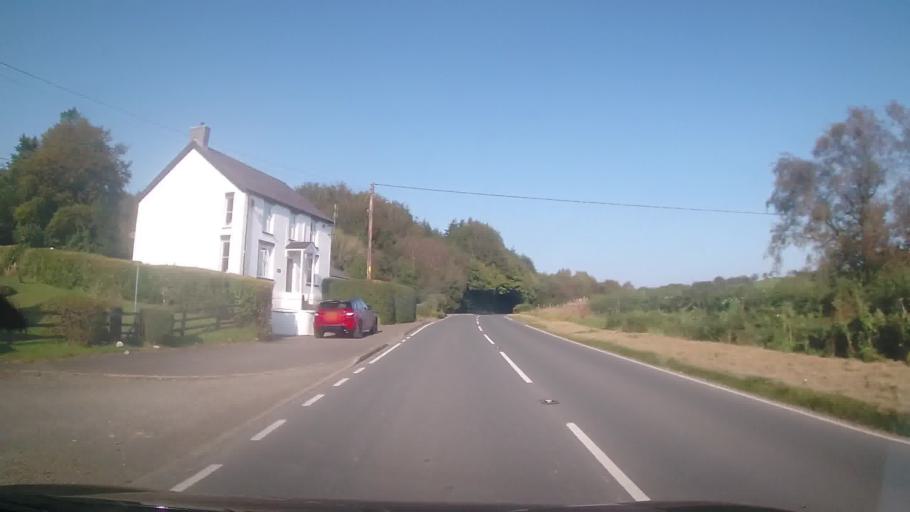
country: GB
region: Wales
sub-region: County of Ceredigion
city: Llangybi
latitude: 52.1770
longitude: -4.0126
